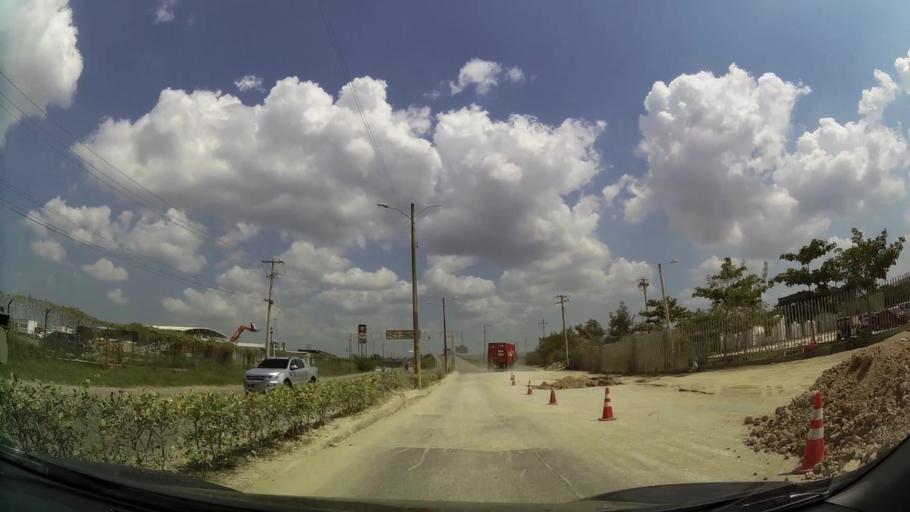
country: CO
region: Bolivar
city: Cartagena
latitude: 10.3427
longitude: -75.4884
